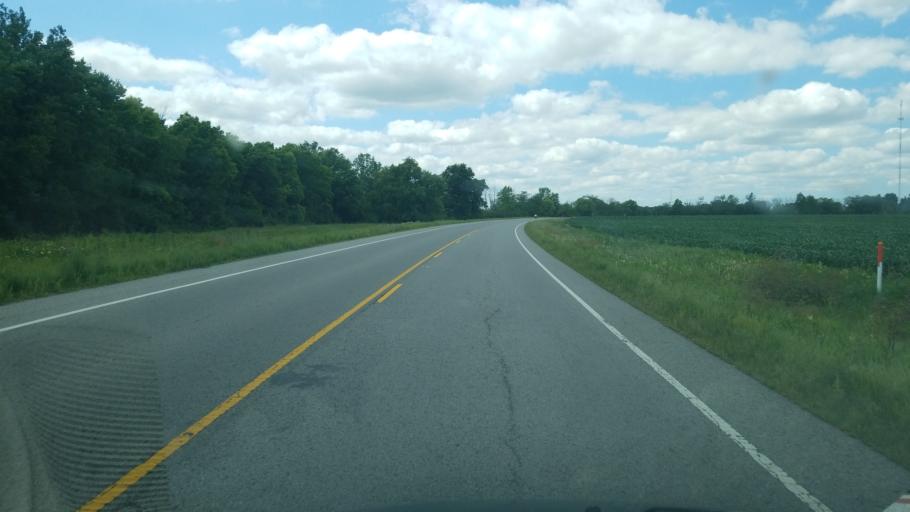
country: US
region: Ohio
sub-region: Henry County
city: Napoleon
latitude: 41.4087
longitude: -84.0792
